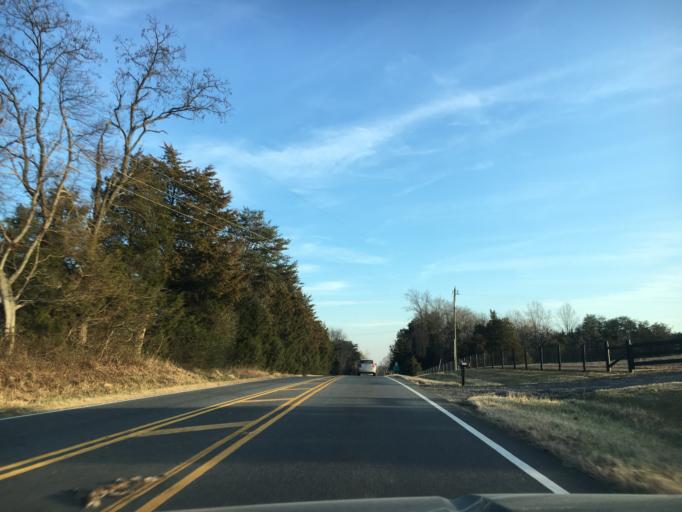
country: US
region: Virginia
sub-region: Culpeper County
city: Merrimac
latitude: 38.5075
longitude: -78.0523
